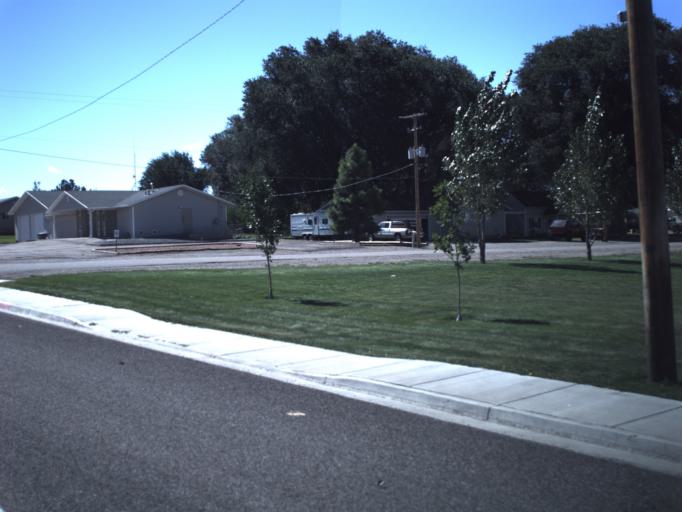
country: US
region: Utah
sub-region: Beaver County
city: Milford
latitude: 38.2129
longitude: -112.9239
